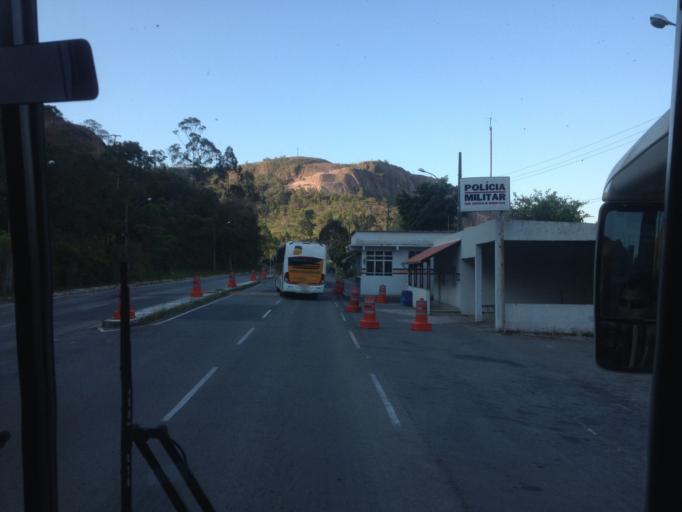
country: BR
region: Minas Gerais
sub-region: Juiz De Fora
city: Juiz de Fora
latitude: -21.6635
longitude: -43.3345
